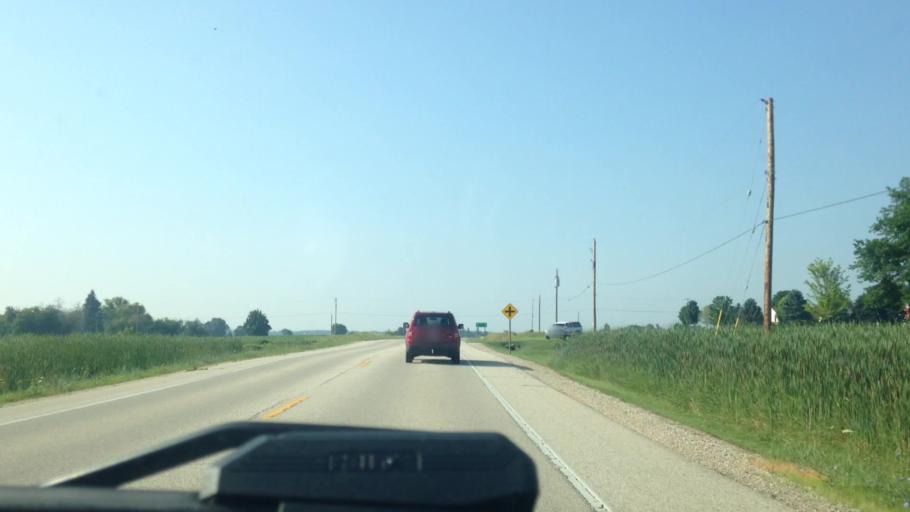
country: US
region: Wisconsin
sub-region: Washington County
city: Slinger
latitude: 43.2840
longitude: -88.2610
